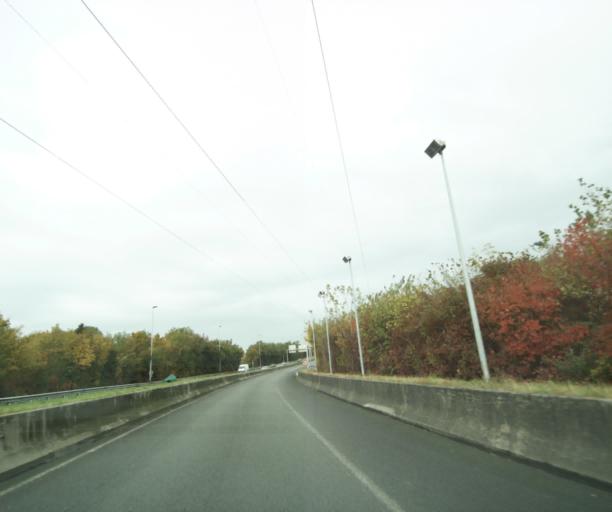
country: FR
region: Nord-Pas-de-Calais
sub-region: Departement du Nord
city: Wasquehal
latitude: 50.6797
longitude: 3.1219
